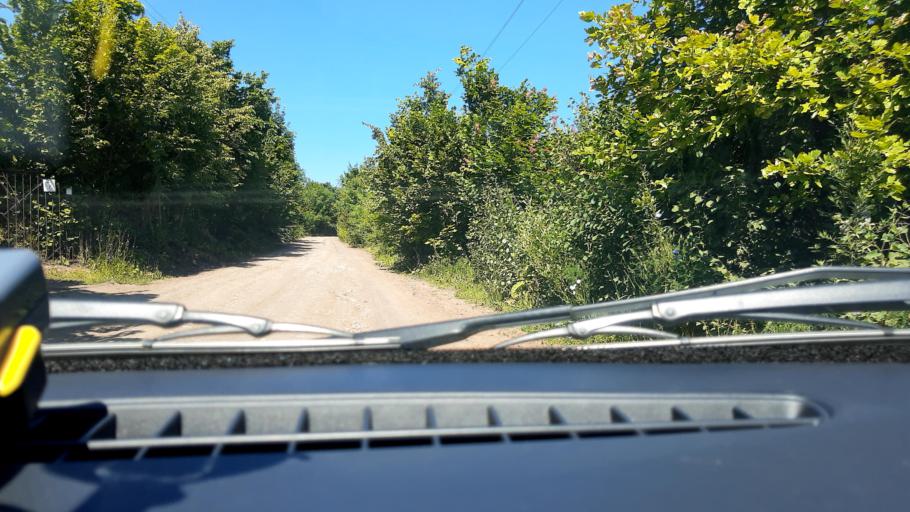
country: RU
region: Bashkortostan
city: Karmaskaly
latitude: 54.3633
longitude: 55.8913
